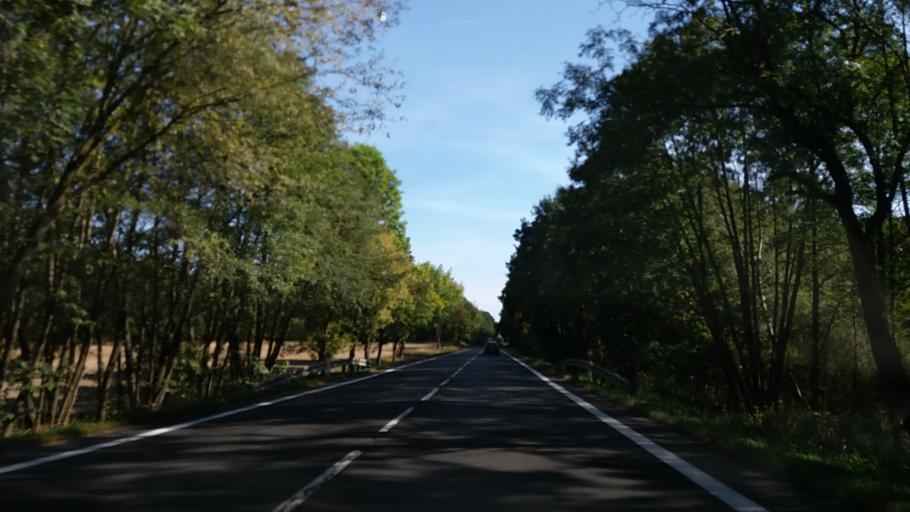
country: PL
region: Greater Poland Voivodeship
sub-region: Powiat miedzychodzki
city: Kwilcz
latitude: 52.5423
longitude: 16.1299
